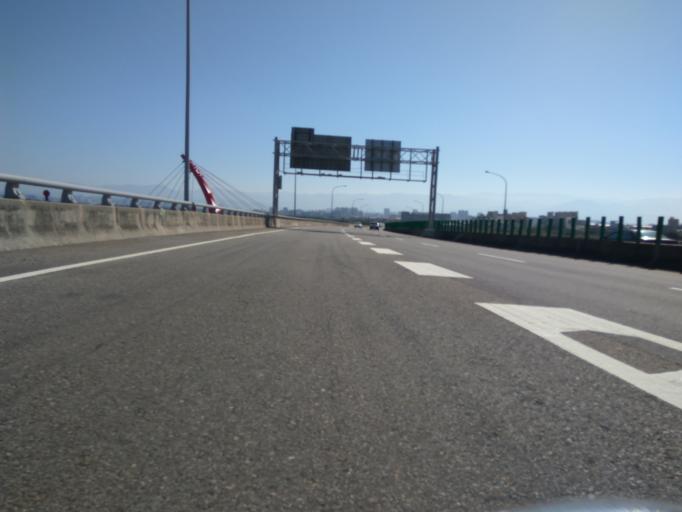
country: TW
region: Taiwan
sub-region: Hsinchu
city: Hsinchu
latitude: 24.8427
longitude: 120.9390
